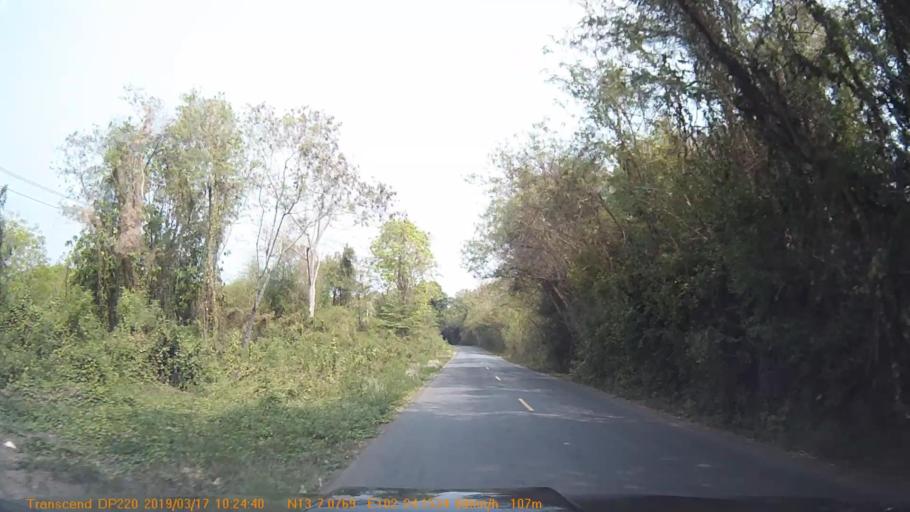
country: TH
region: Chanthaburi
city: Soi Dao
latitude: 13.1183
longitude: 102.4024
